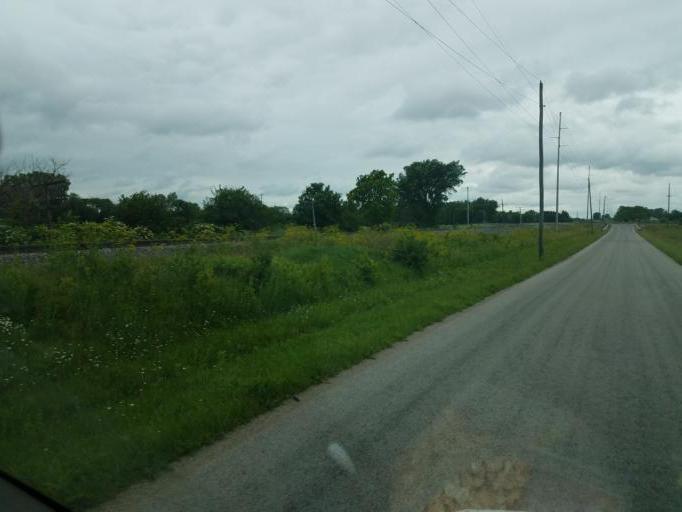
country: US
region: Ohio
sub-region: Morrow County
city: Mount Gilead
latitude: 40.5440
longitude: -82.8726
